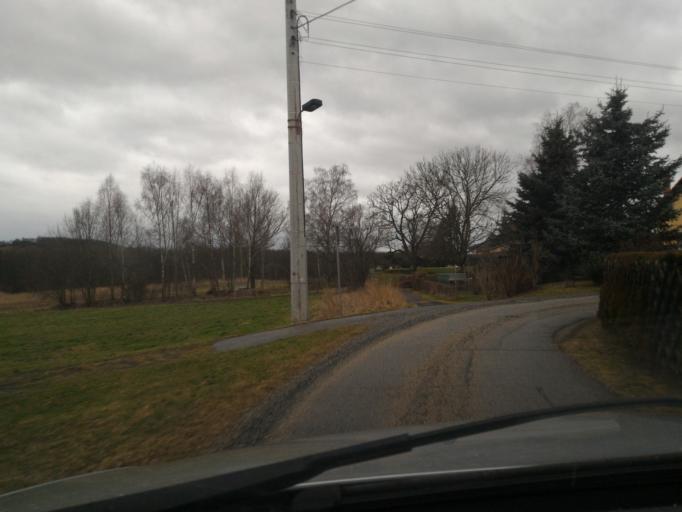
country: DE
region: Saxony
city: Leutersdorf
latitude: 50.9510
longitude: 14.6446
